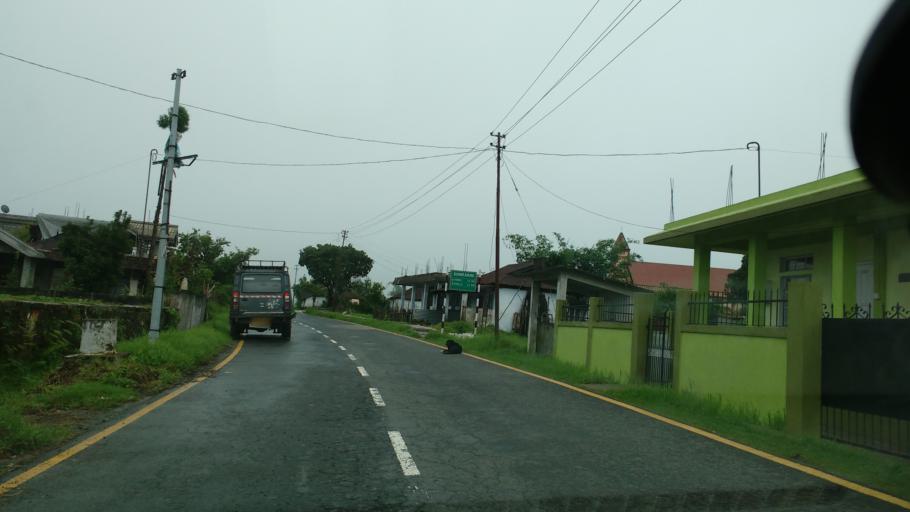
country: IN
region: Meghalaya
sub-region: East Khasi Hills
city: Cherrapunji
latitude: 25.3492
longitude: 91.7391
